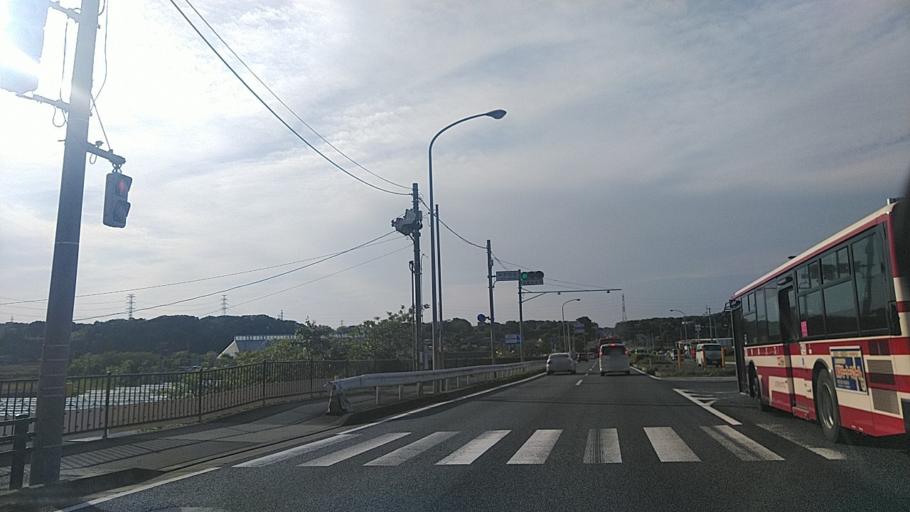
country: JP
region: Chiba
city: Shiroi
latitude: 35.7572
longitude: 140.1094
